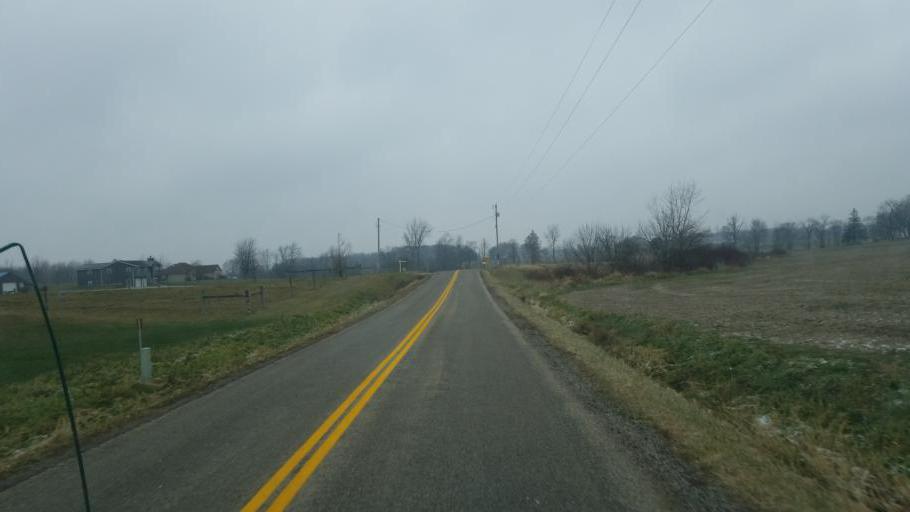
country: US
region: Ohio
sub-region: Huron County
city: New London
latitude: 41.0129
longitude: -82.3549
